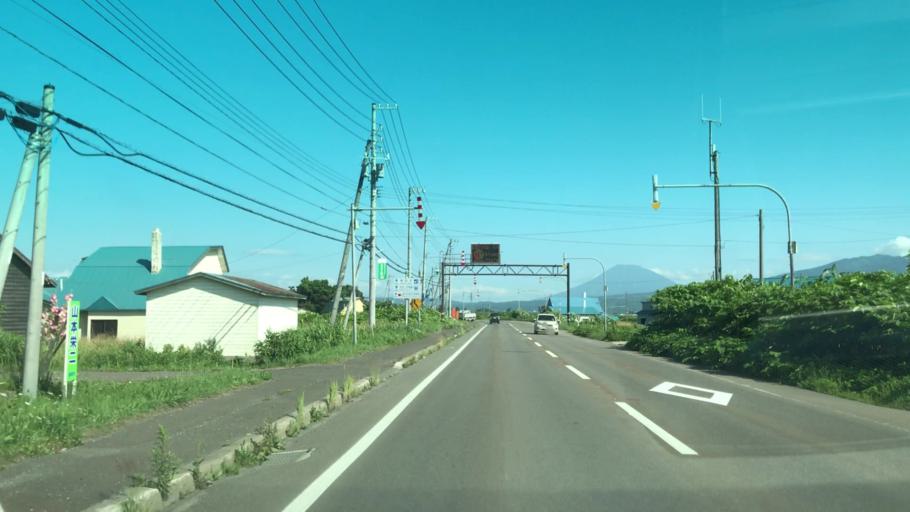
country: JP
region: Hokkaido
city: Iwanai
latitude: 43.0305
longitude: 140.5382
